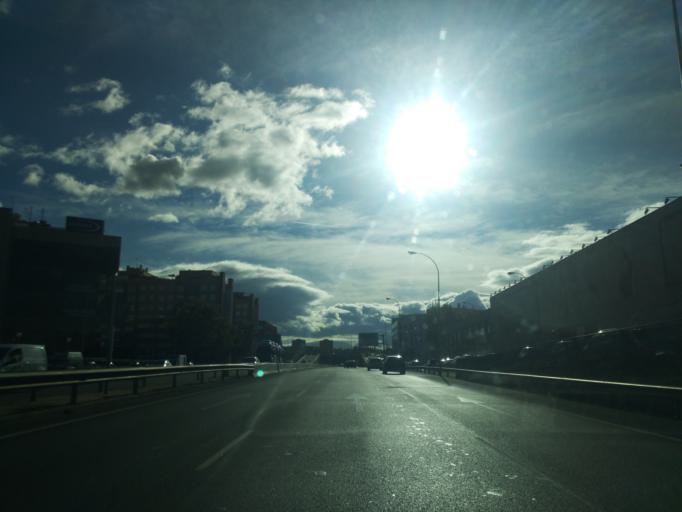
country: ES
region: Madrid
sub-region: Provincia de Madrid
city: Usera
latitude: 40.3797
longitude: -3.6924
